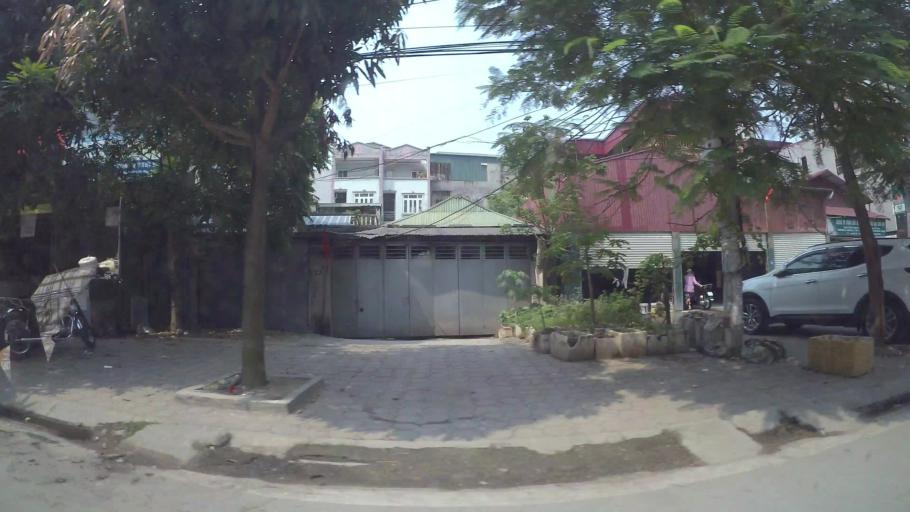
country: VN
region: Ha Noi
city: Van Dien
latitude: 20.9634
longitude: 105.8218
